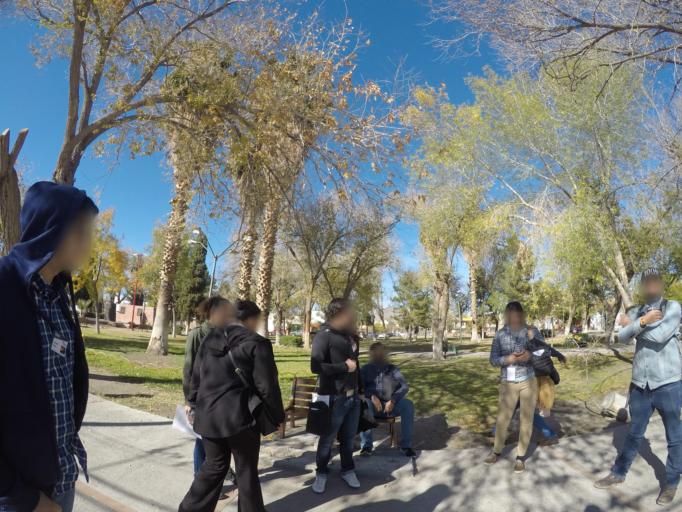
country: MX
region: Chihuahua
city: Ciudad Juarez
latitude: 31.7443
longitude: -106.4607
